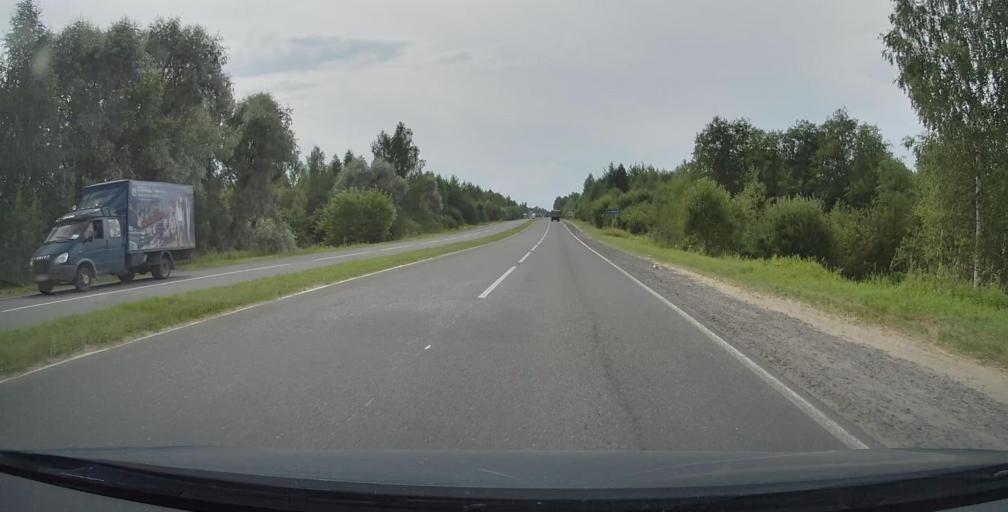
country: RU
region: Jaroslavl
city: Rybinsk
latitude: 58.0083
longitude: 38.9123
